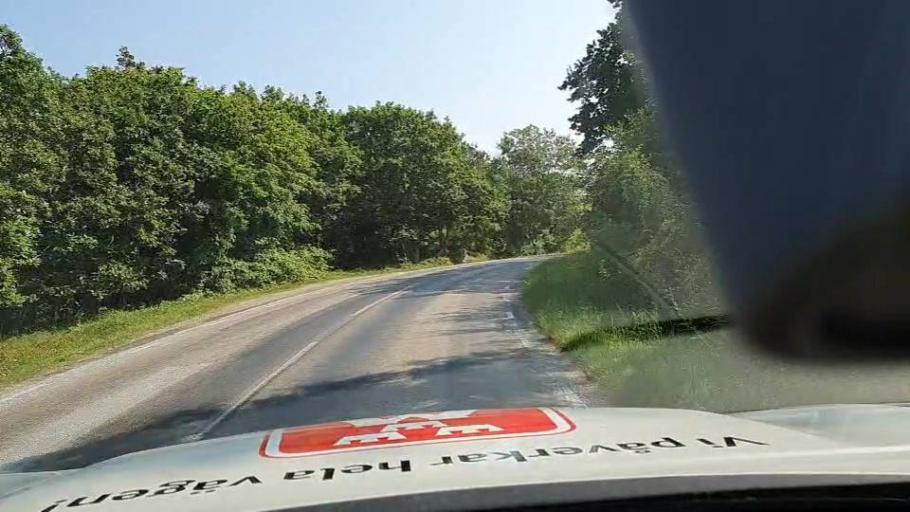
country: SE
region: Vaestra Goetaland
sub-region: Tjorns Kommun
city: Skaerhamn
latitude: 58.0881
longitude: 11.4870
